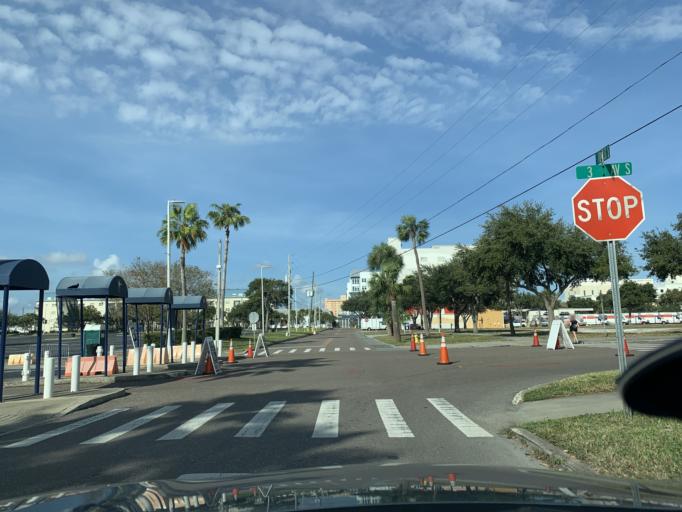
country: US
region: Florida
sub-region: Pinellas County
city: Saint Petersburg
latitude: 27.7683
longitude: -82.6482
